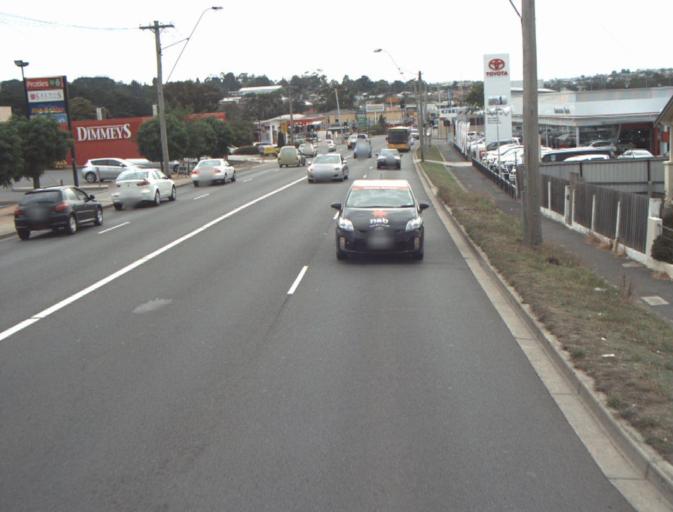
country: AU
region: Tasmania
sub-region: Launceston
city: East Launceston
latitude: -41.4637
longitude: 147.1580
